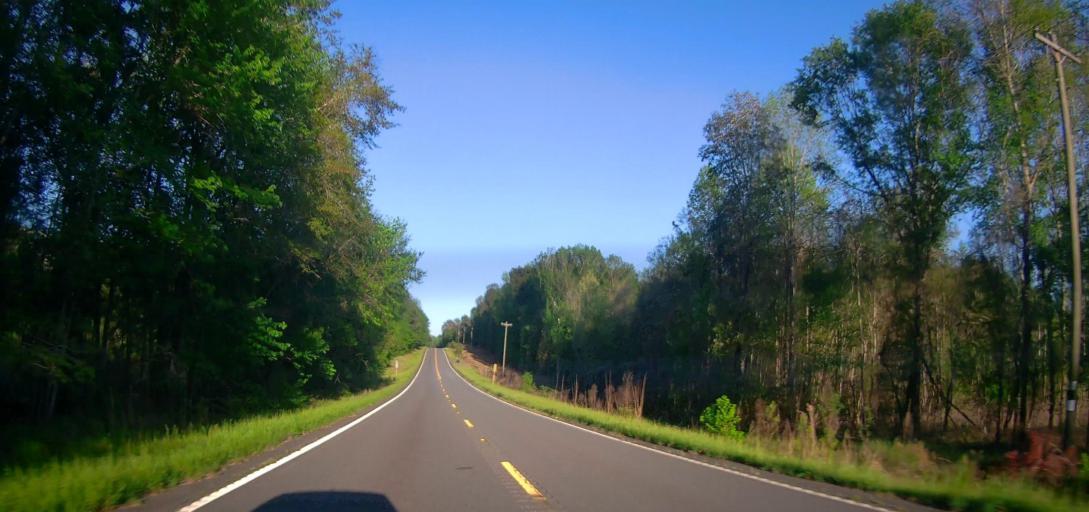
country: US
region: Georgia
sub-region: Schley County
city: Ellaville
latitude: 32.3217
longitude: -84.3108
